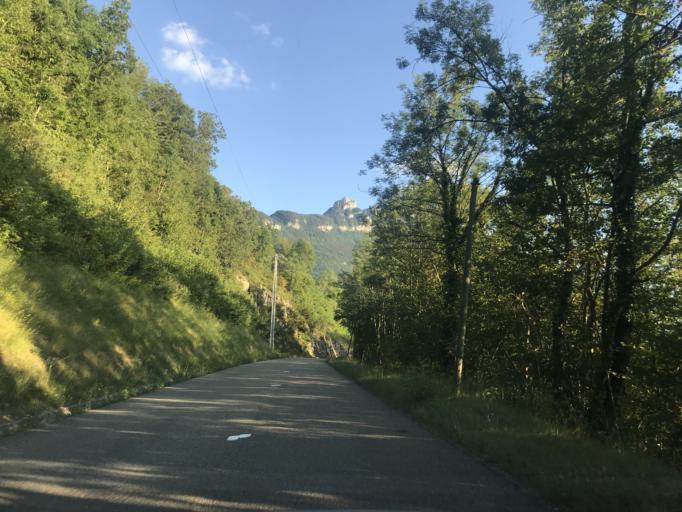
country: FR
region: Rhone-Alpes
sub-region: Departement de la Savoie
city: Brison-Saint-Innocent
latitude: 45.7064
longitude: 5.8296
